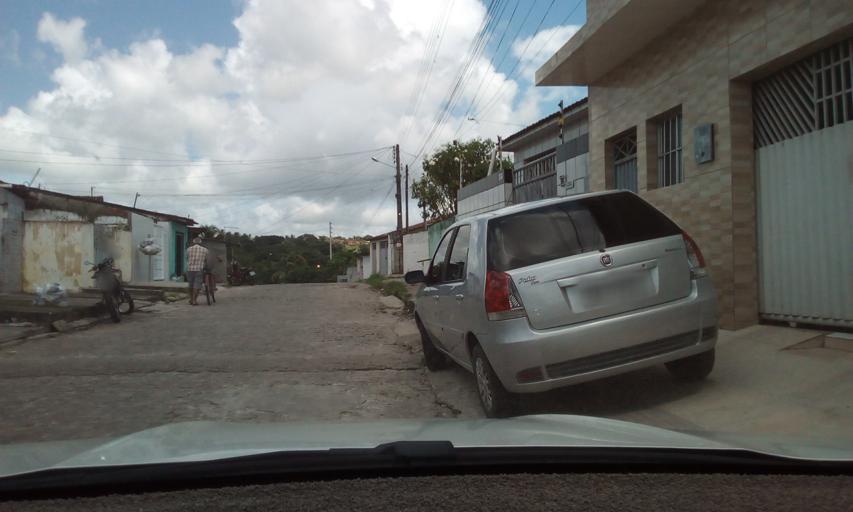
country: BR
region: Paraiba
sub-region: Bayeux
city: Bayeux
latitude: -7.1361
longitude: -34.9240
